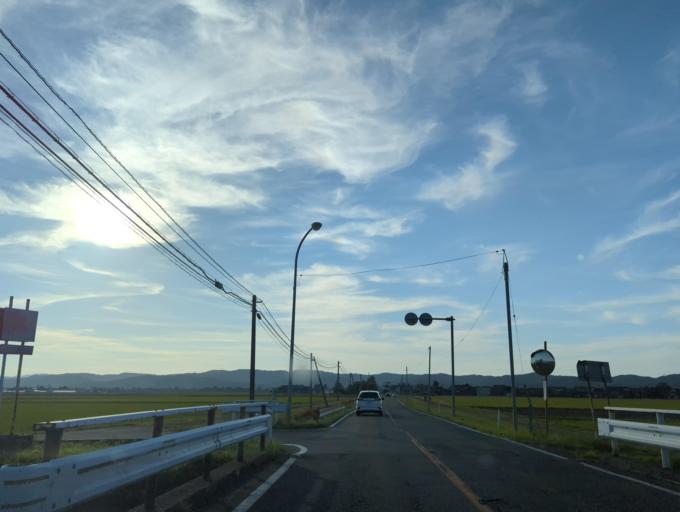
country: JP
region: Niigata
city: Mitsuke
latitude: 37.5554
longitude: 138.8429
